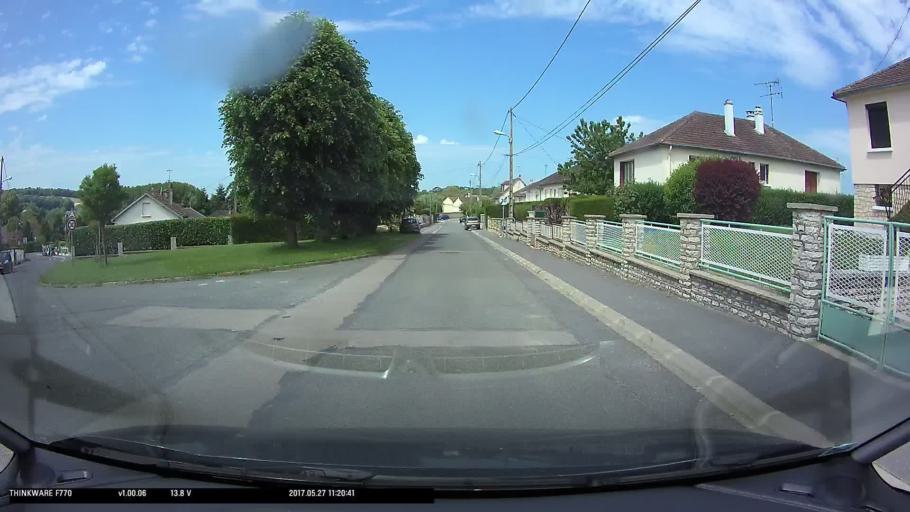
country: FR
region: Picardie
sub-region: Departement de l'Oise
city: Trie-Chateau
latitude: 49.2881
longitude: 1.8217
